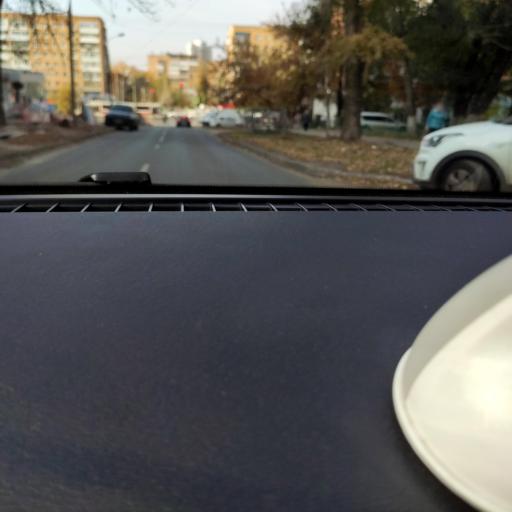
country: RU
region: Samara
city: Samara
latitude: 53.2095
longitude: 50.1419
